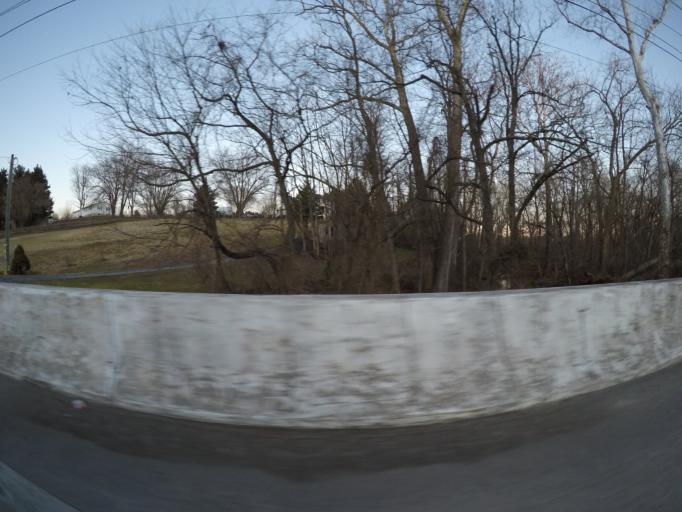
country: US
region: Maryland
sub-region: Cecil County
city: Rising Sun
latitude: 39.7062
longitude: -76.0632
